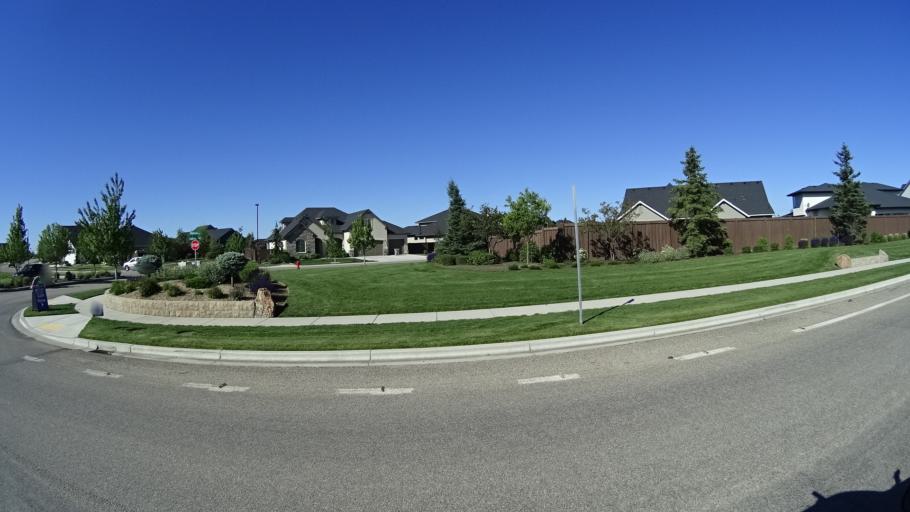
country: US
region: Idaho
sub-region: Ada County
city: Star
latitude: 43.6600
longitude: -116.4433
